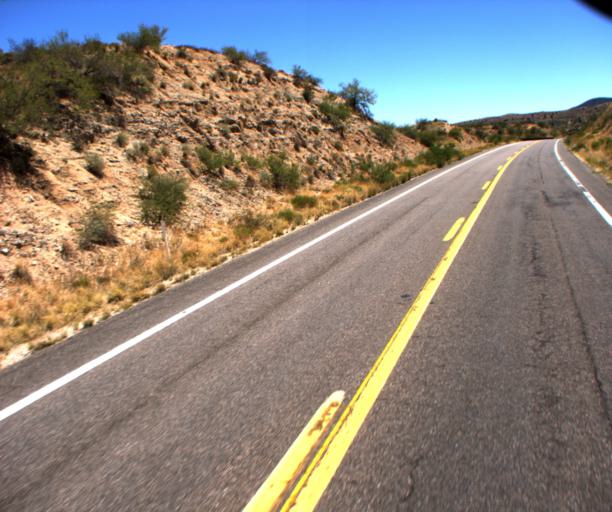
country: US
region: Arizona
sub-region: Gila County
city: Globe
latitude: 33.3420
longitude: -110.7287
